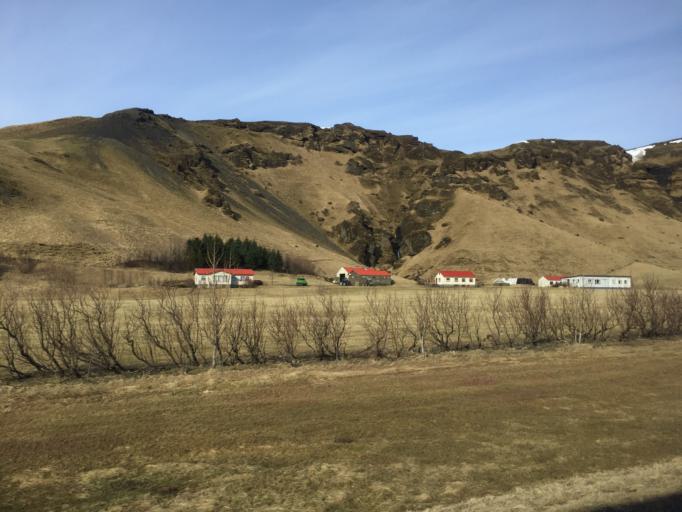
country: IS
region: South
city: Vestmannaeyjar
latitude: 63.4542
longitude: -19.0839
